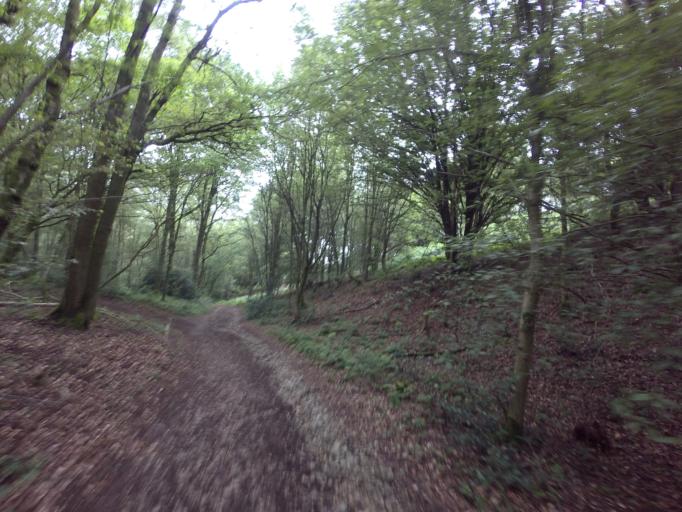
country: BE
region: Wallonia
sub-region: Province de Liege
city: Plombieres
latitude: 50.7668
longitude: 5.9782
